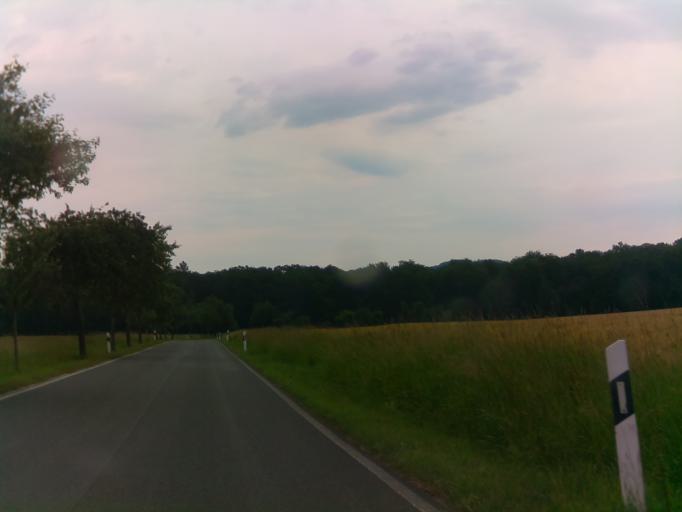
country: DE
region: Lower Saxony
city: Heinsen
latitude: 51.8953
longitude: 9.4300
